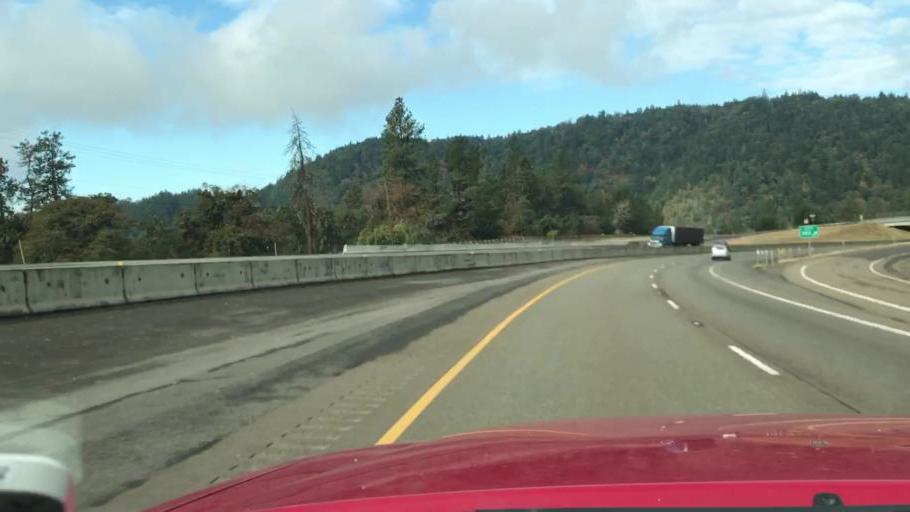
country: US
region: Oregon
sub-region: Douglas County
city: Riddle
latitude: 42.9480
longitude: -123.3269
